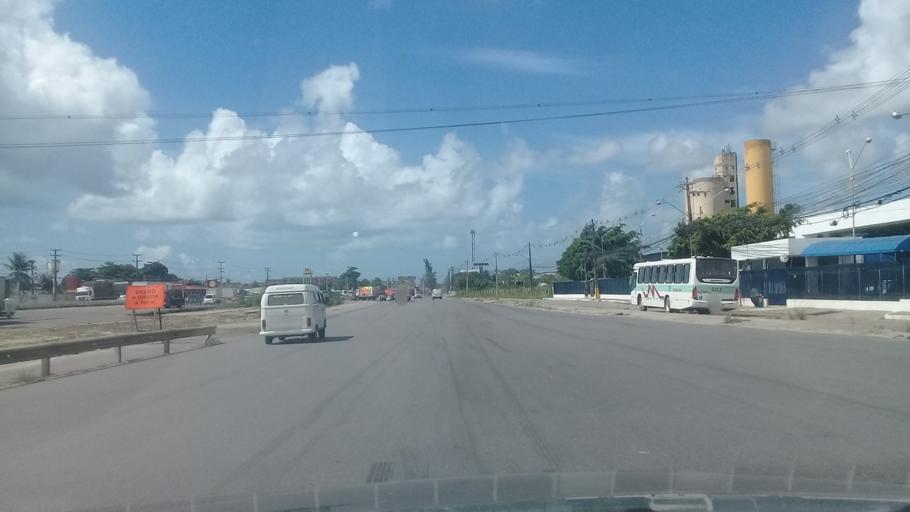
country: BR
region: Pernambuco
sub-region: Jaboatao Dos Guararapes
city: Jaboatao
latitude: -8.1554
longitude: -34.9419
